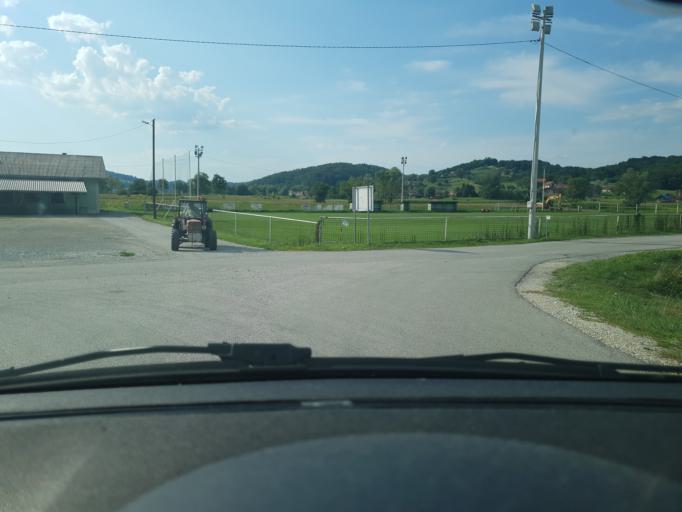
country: HR
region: Krapinsko-Zagorska
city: Zabok
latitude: 46.0359
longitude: 15.8262
